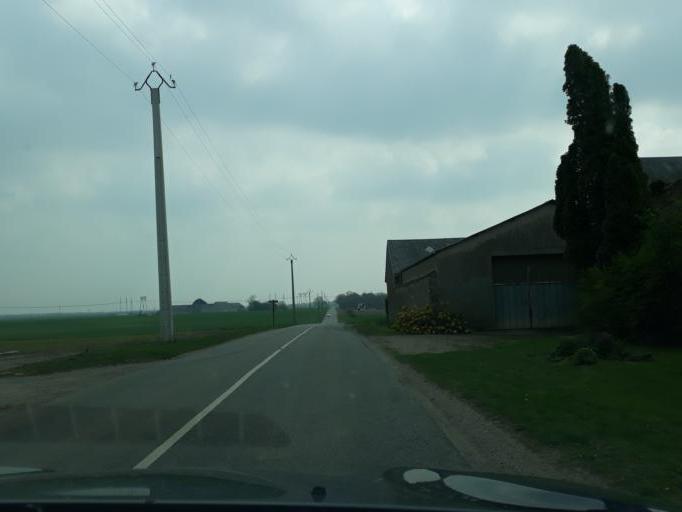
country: FR
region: Centre
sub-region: Departement du Loiret
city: Bricy
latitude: 48.0105
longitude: 1.8083
